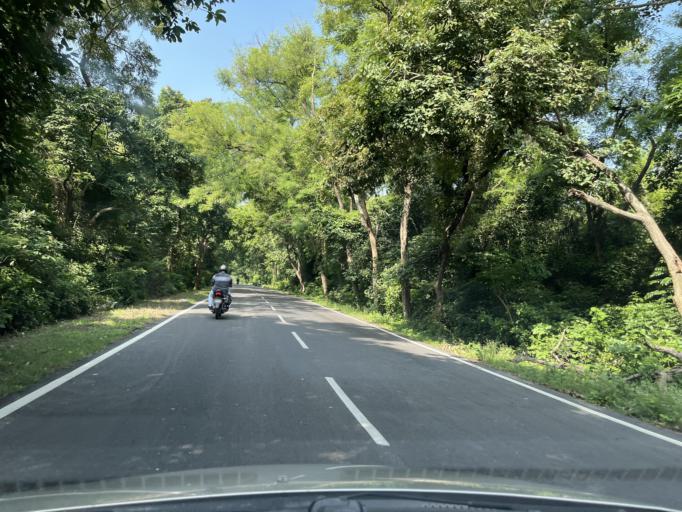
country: IN
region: Uttarakhand
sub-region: Naini Tal
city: Kaladhungi
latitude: 29.2247
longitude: 79.2433
